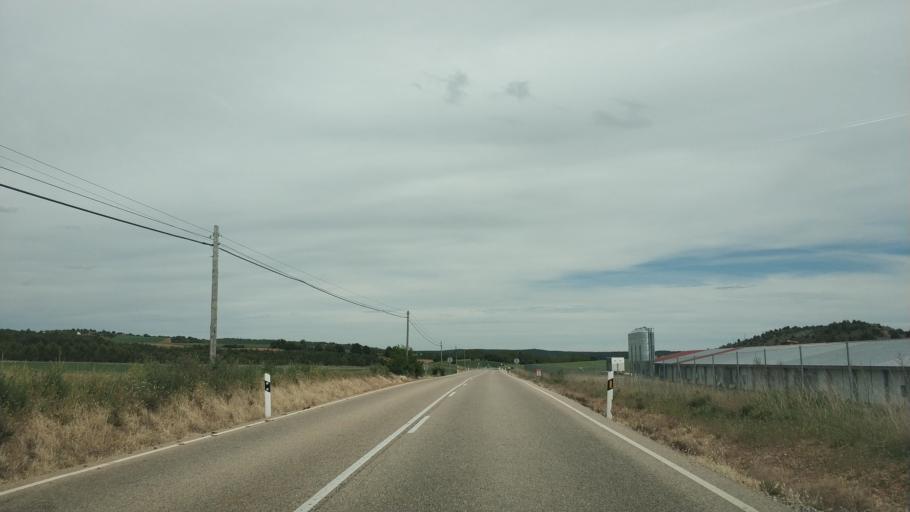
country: ES
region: Castille and Leon
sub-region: Provincia de Soria
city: El Burgo de Osma
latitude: 41.5757
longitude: -3.0252
